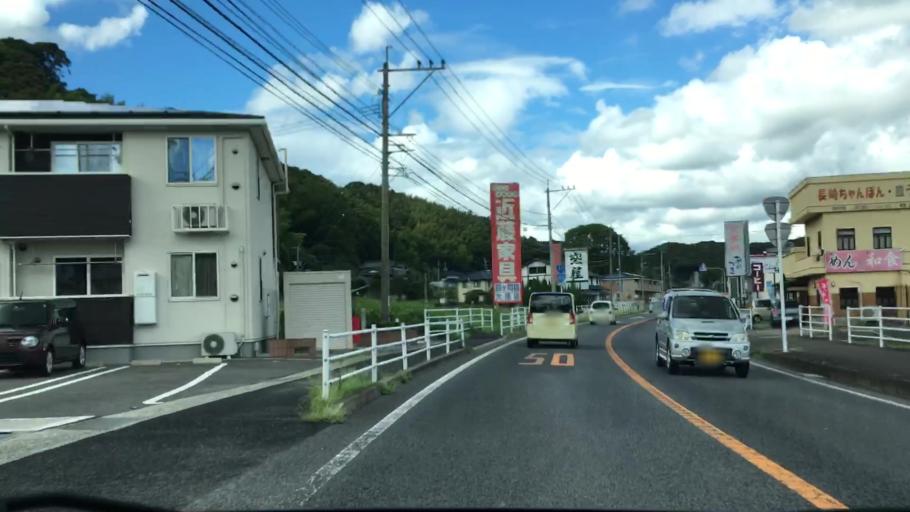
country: JP
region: Nagasaki
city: Sasebo
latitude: 33.1587
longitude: 129.8308
